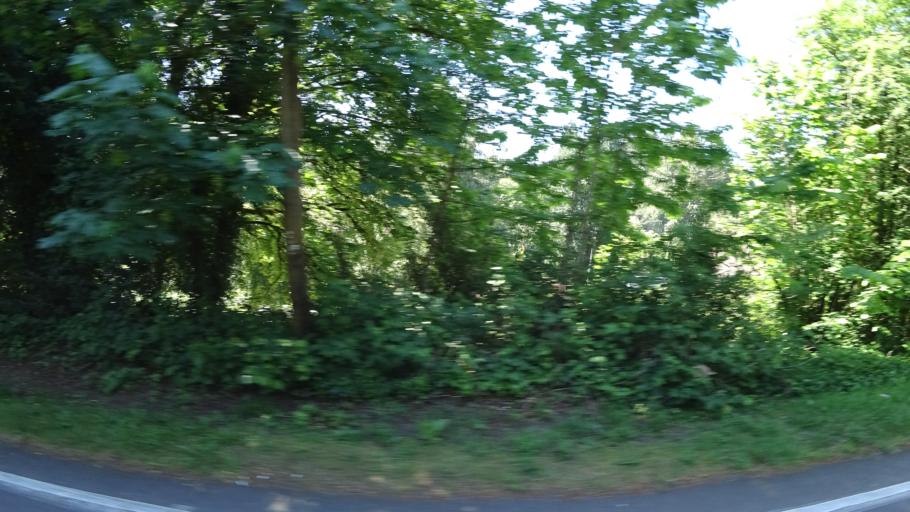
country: US
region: Oregon
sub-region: Clackamas County
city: Happy Valley
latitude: 45.4725
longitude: -122.5251
